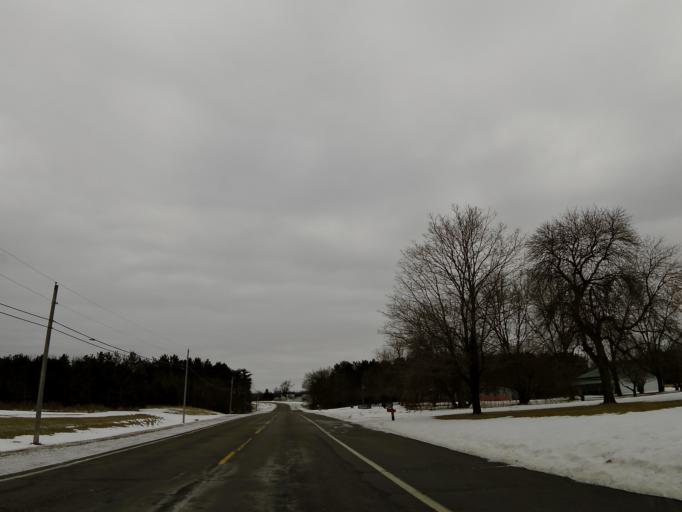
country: US
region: Minnesota
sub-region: Washington County
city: Cottage Grove
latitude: 44.8105
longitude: -92.8934
